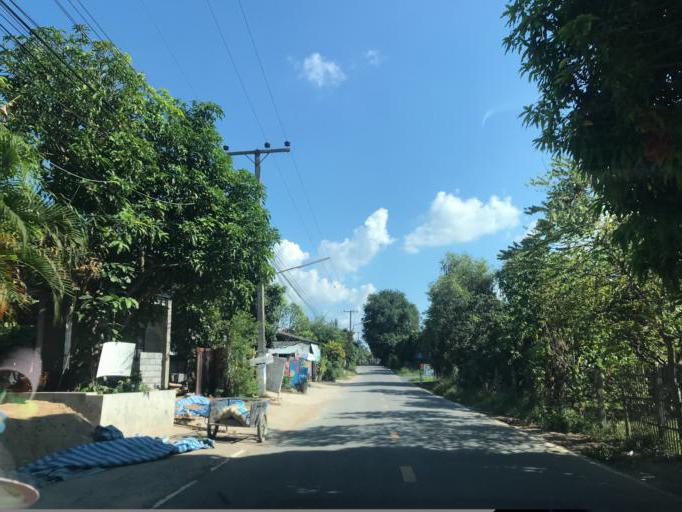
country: TH
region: Chiang Mai
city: Mae Wang
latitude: 18.5574
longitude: 98.8300
